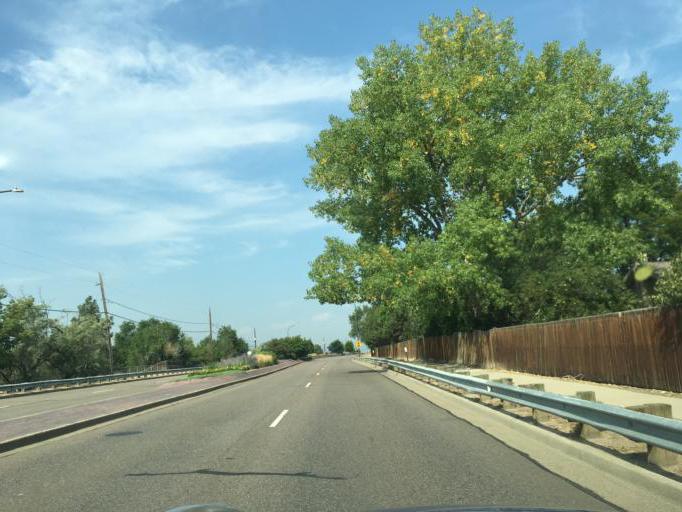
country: US
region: Colorado
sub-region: Adams County
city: Westminster
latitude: 39.8412
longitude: -105.0676
